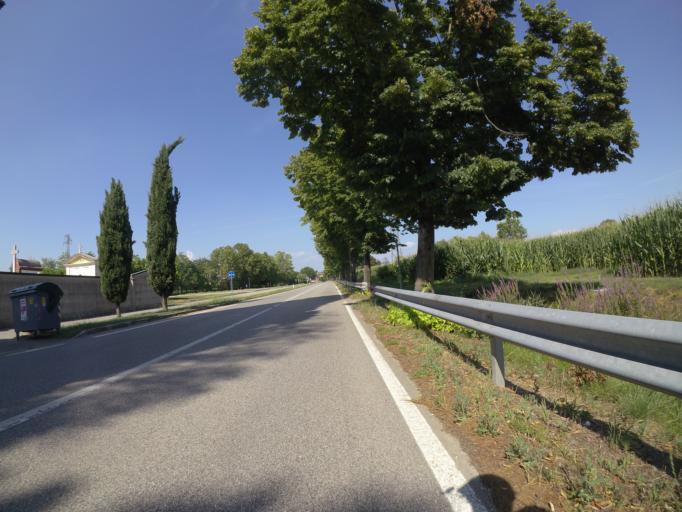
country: IT
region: Friuli Venezia Giulia
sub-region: Provincia di Udine
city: Lestizza
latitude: 45.9516
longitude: 13.1382
